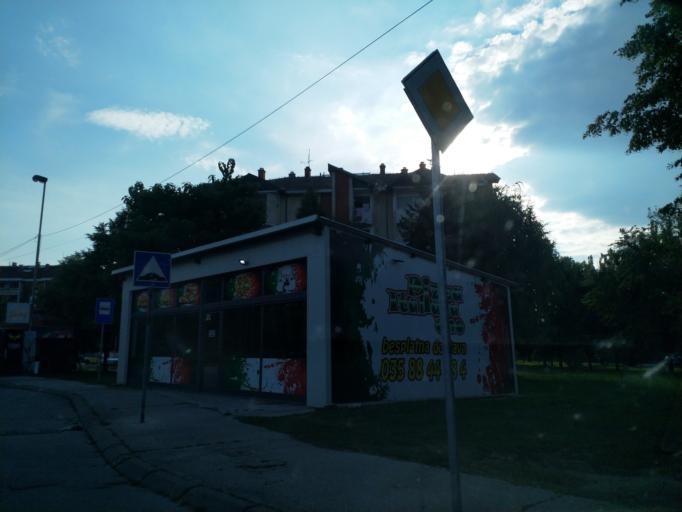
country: RS
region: Central Serbia
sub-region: Pomoravski Okrug
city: Jagodina
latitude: 43.9866
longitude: 21.2457
